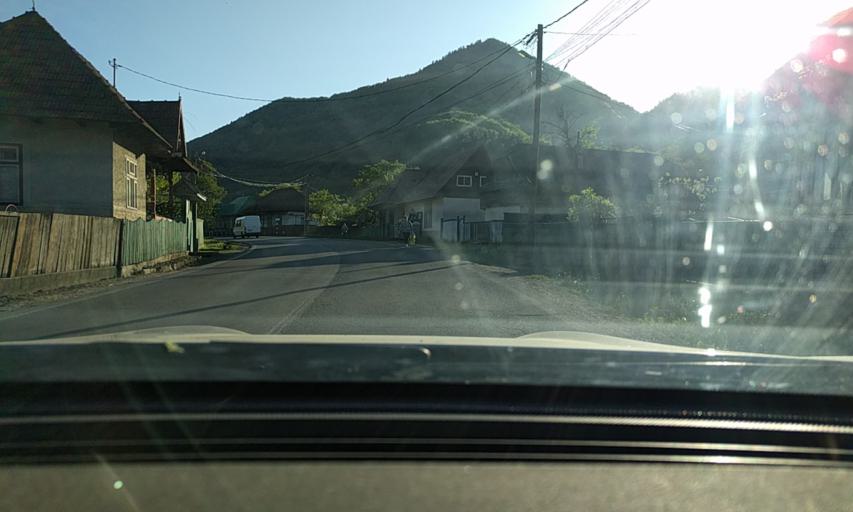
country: RO
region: Bacau
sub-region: Oras Slanic-Moldova
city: Slanic-Moldova
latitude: 46.1675
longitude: 26.4724
